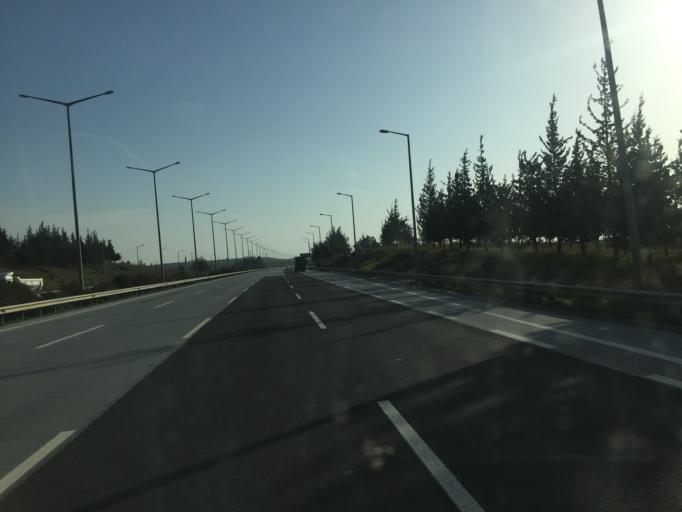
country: TR
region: Mersin
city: Yenice
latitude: 37.0234
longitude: 35.0571
